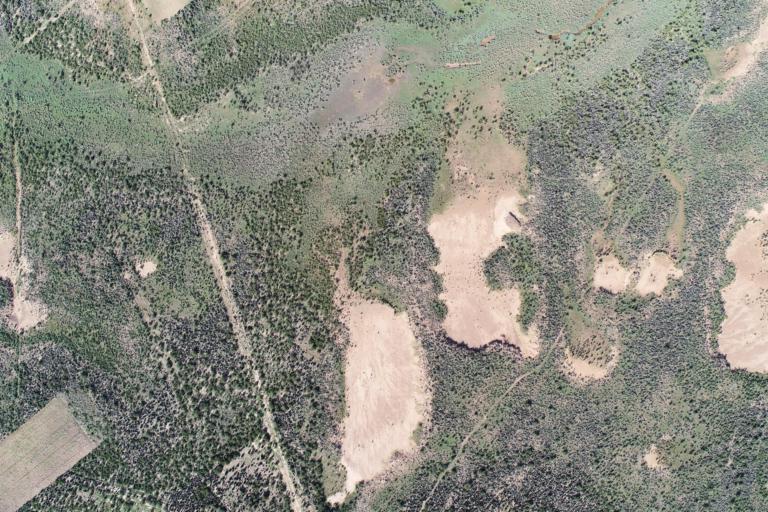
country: BO
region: La Paz
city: Curahuara de Carangas
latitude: -17.3008
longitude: -68.5000
